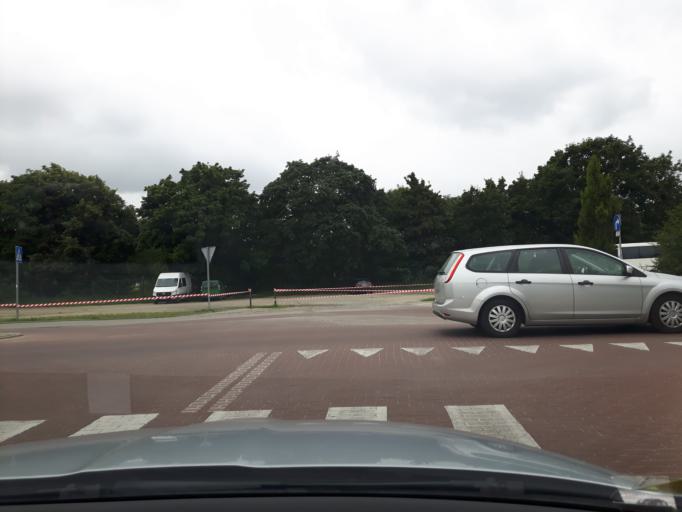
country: PL
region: Pomeranian Voivodeship
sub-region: Sopot
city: Sopot
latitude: 54.4292
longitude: 18.5746
